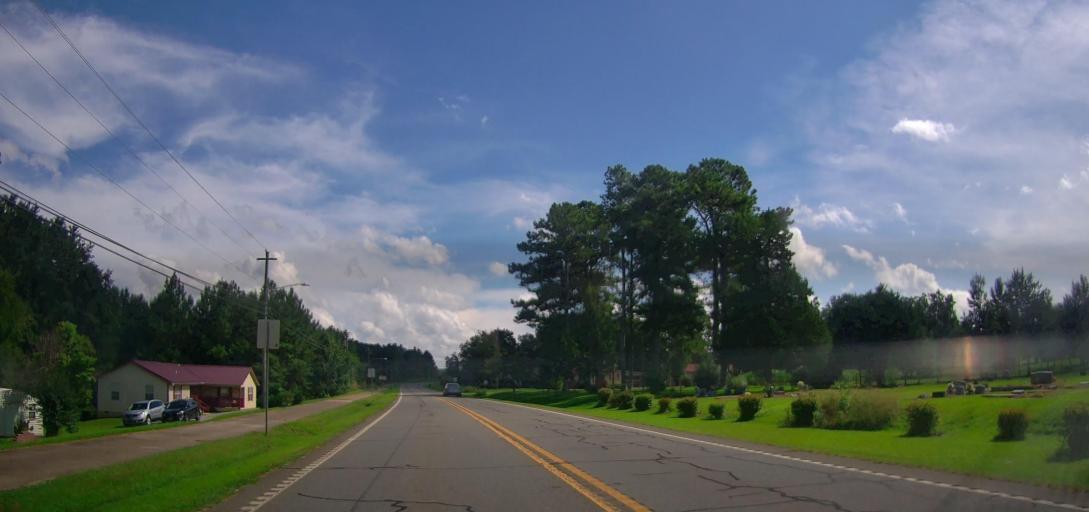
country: US
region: Georgia
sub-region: Talbot County
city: Sardis
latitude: 32.7807
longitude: -84.5593
